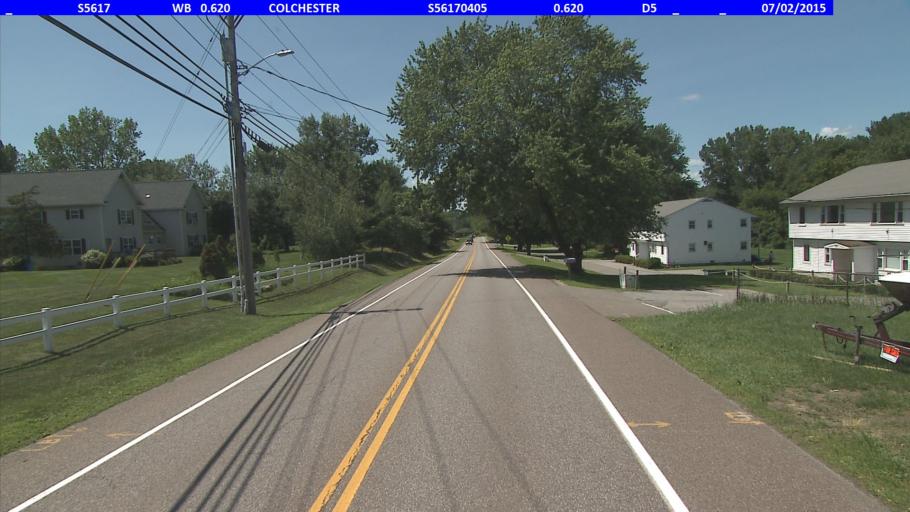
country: US
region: Vermont
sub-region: Chittenden County
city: Colchester
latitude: 44.5527
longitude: -73.1790
